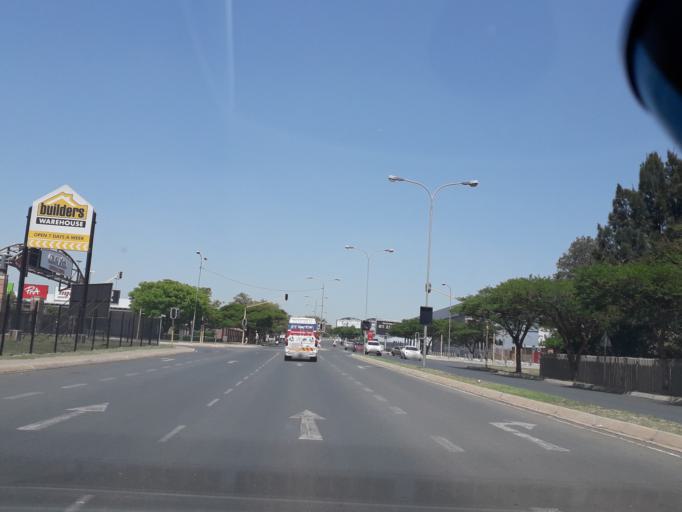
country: ZA
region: Gauteng
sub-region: City of Tshwane Metropolitan Municipality
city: Centurion
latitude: -25.8748
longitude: 28.1656
